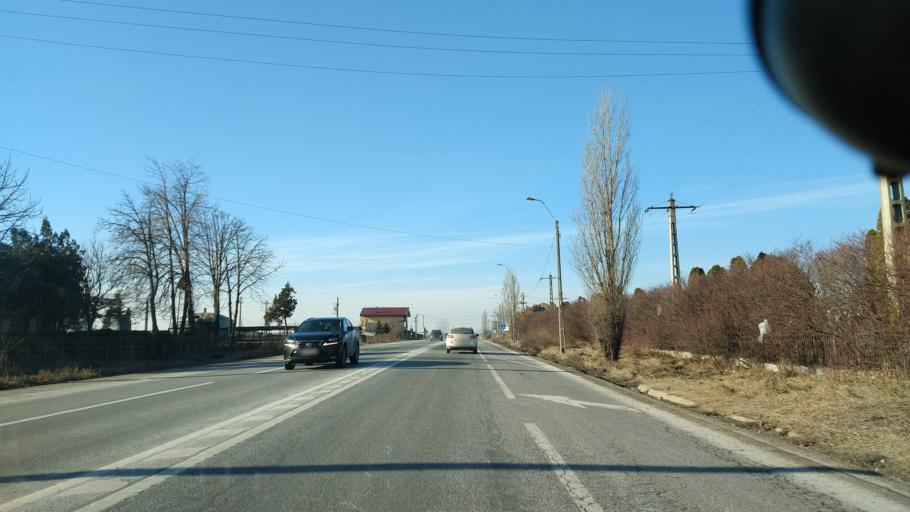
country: RO
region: Iasi
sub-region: Comuna Letcani
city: Letcani
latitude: 47.1855
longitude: 27.4517
